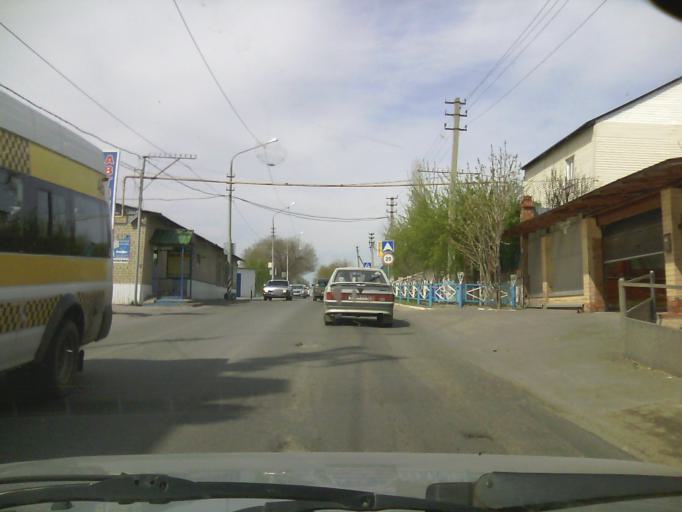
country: RU
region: Saratov
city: Sokolovyy
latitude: 51.5766
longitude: 45.8997
